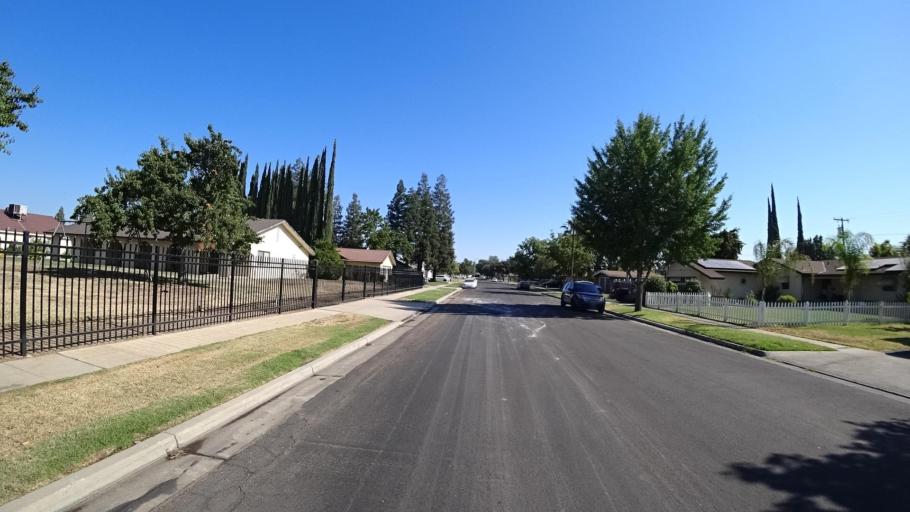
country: US
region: California
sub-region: Fresno County
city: Fresno
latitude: 36.7825
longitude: -119.7703
